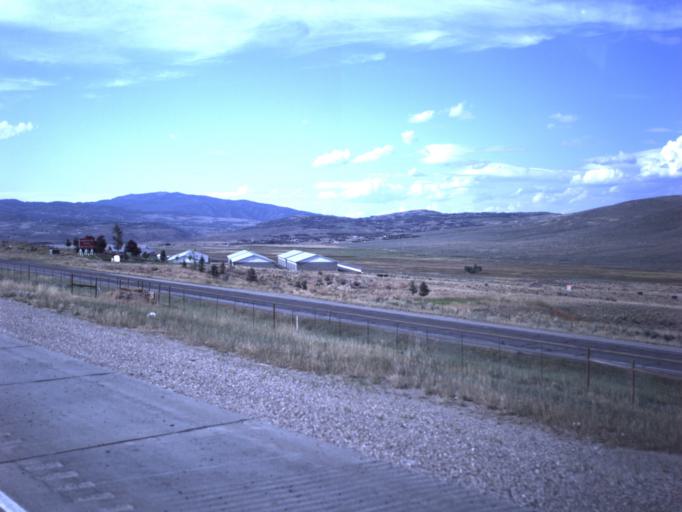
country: US
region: Utah
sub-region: Summit County
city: Park City
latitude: 40.6927
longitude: -111.4687
